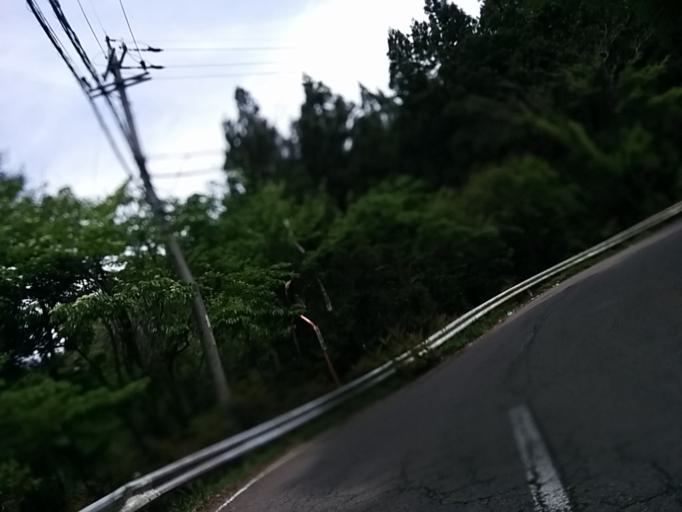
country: JP
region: Gifu
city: Gujo
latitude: 35.7350
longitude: 136.9565
